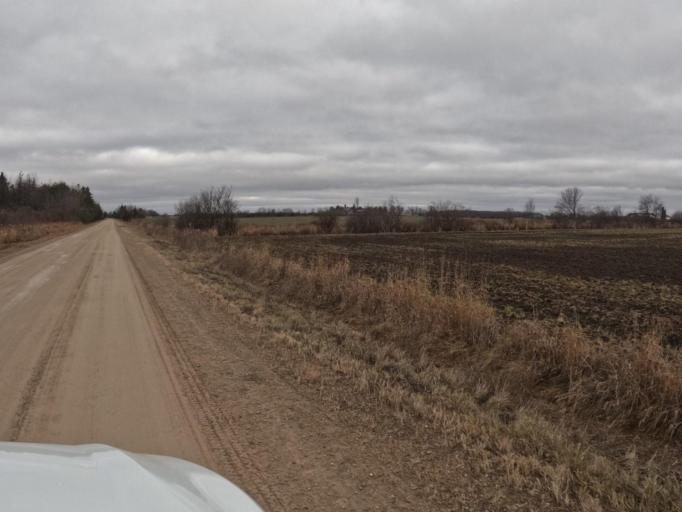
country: CA
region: Ontario
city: Shelburne
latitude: 43.9513
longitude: -80.3969
